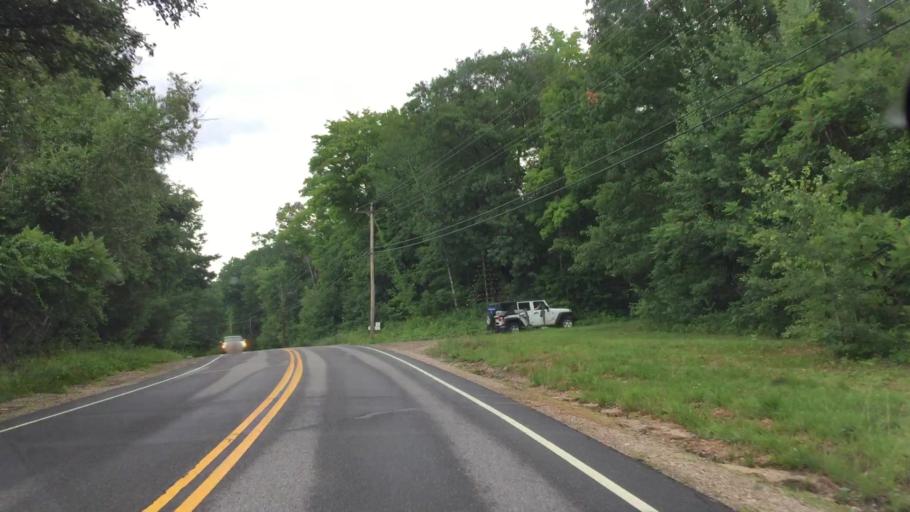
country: US
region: New Hampshire
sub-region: Carroll County
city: Center Harbor
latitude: 43.7462
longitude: -71.4781
